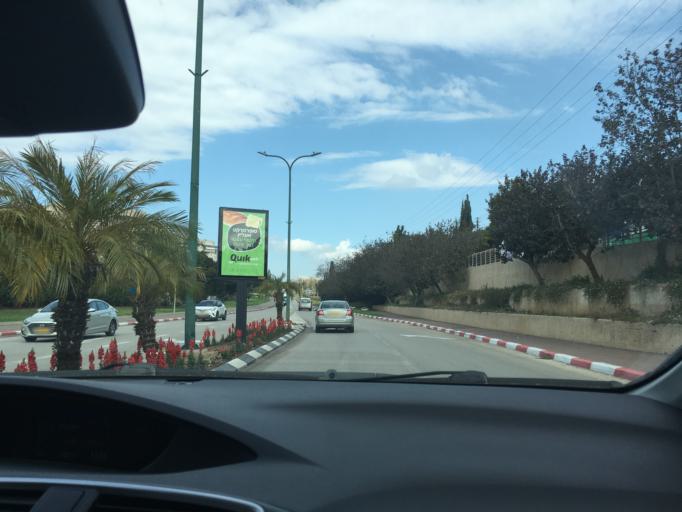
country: IL
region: Tel Aviv
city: Ramat HaSharon
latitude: 32.1625
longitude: 34.8531
